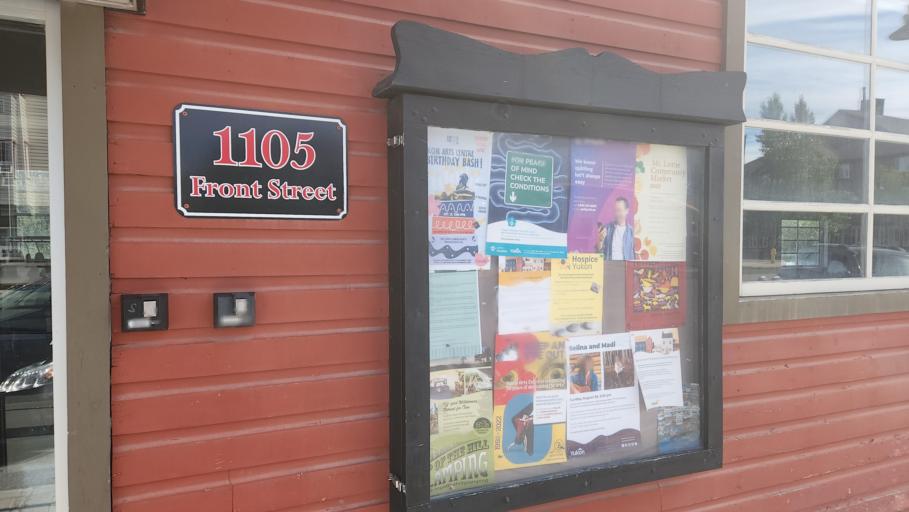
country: CA
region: Yukon
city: Whitehorse
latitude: 60.7198
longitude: -135.0498
